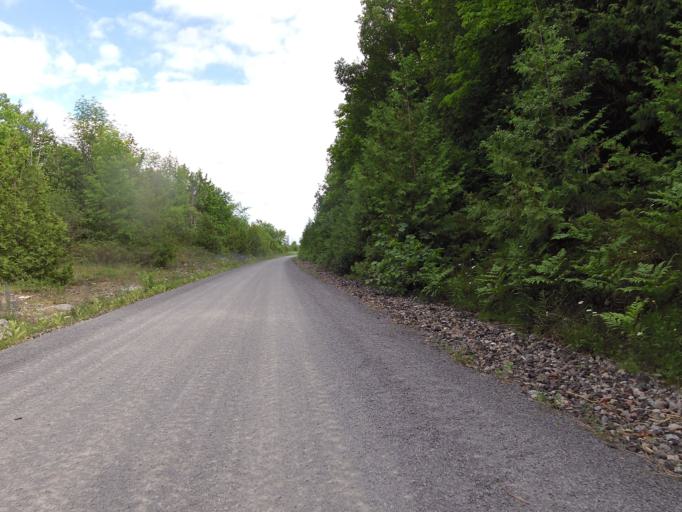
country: CA
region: Ontario
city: Arnprior
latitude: 45.3014
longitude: -76.2662
